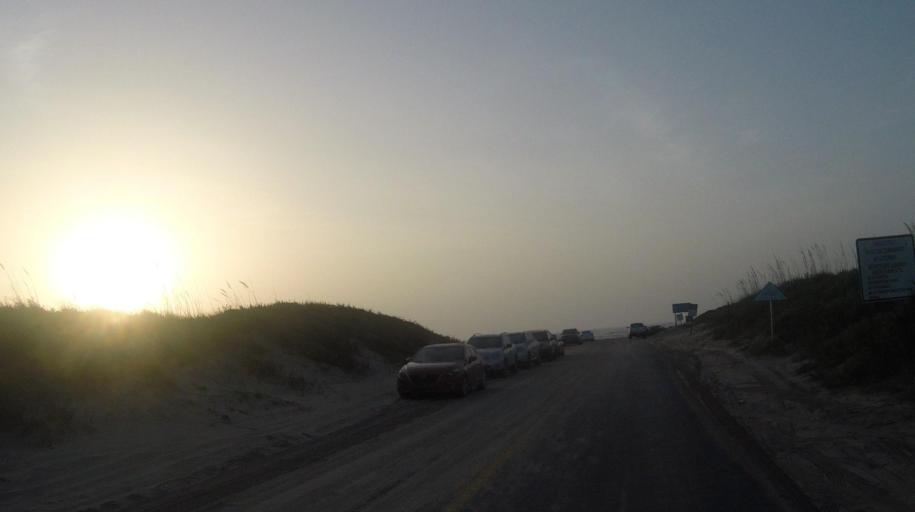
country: US
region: Texas
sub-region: Cameron County
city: Port Isabel
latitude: 25.9970
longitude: -97.1517
